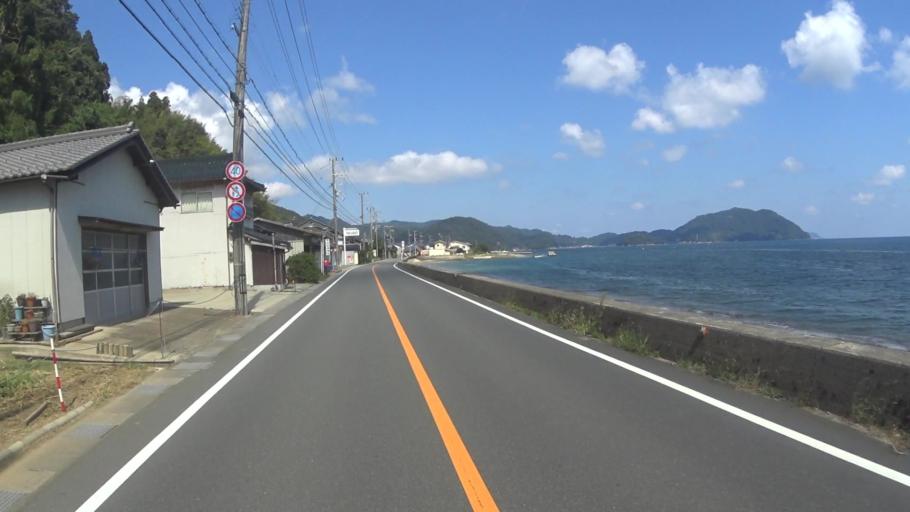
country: JP
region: Kyoto
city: Miyazu
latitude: 35.6530
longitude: 135.2561
